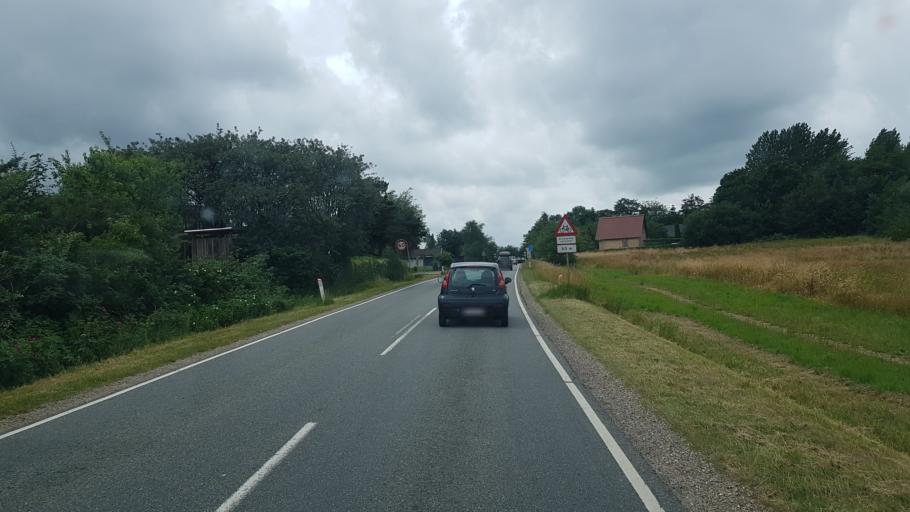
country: DK
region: South Denmark
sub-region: Vejen Kommune
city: Vejen
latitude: 55.4252
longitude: 9.1565
